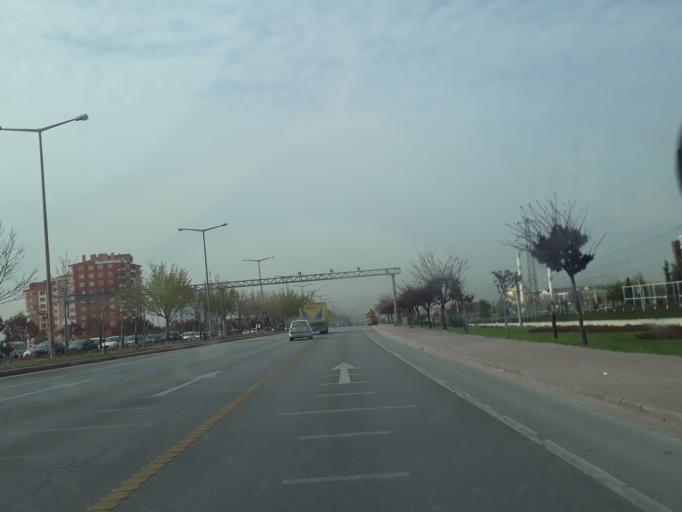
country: TR
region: Konya
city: Asagipinarbasi
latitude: 37.9932
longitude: 32.5186
